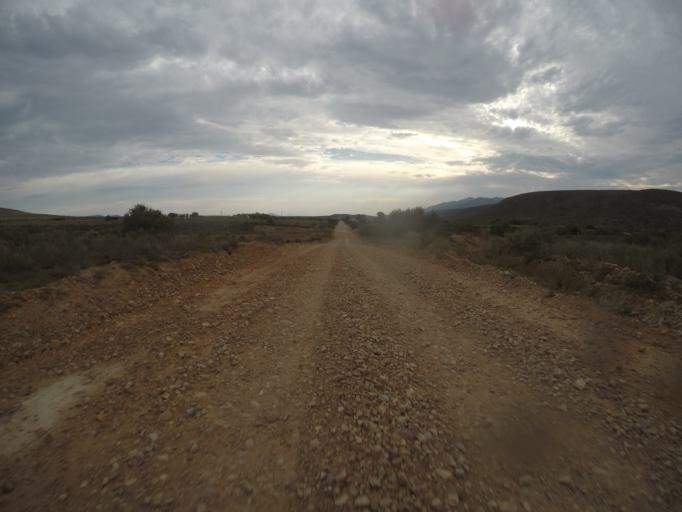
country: ZA
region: Eastern Cape
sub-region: Cacadu District Municipality
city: Willowmore
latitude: -33.4914
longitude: 23.5982
